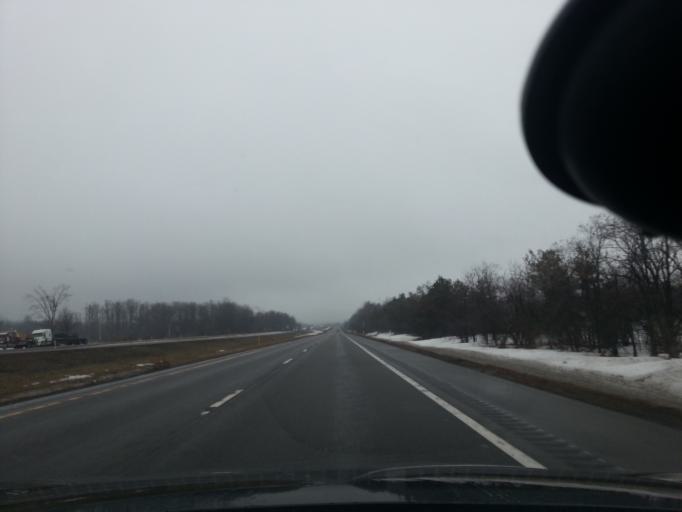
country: US
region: New York
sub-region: Jefferson County
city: Watertown
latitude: 43.9367
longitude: -75.9639
